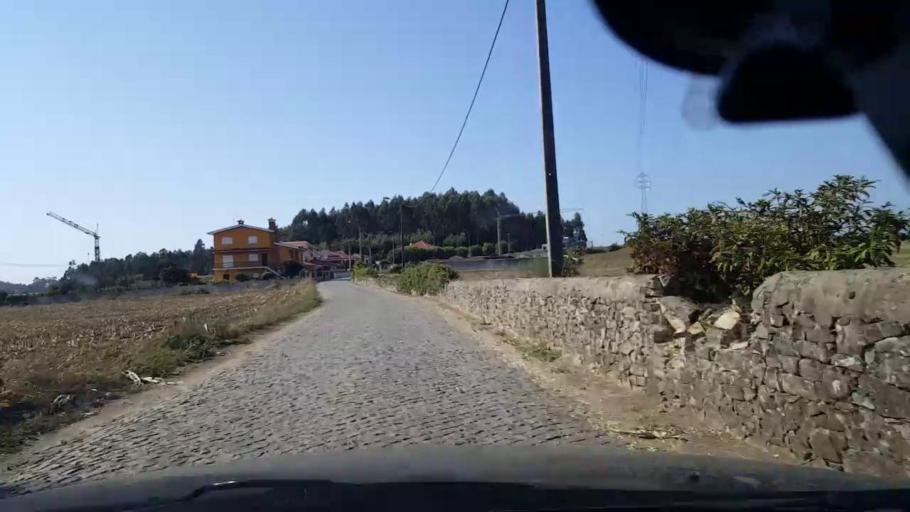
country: PT
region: Porto
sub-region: Vila do Conde
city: Arvore
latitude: 41.3538
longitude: -8.7056
